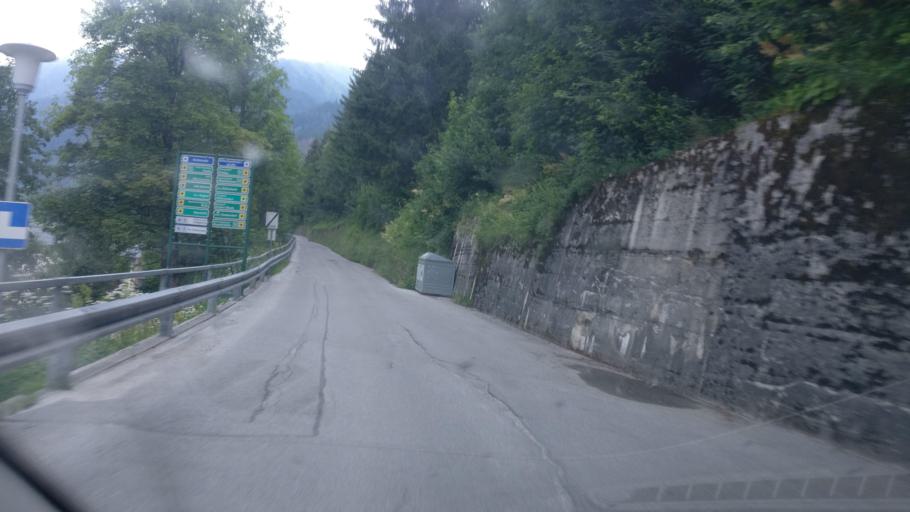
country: AT
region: Salzburg
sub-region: Politischer Bezirk Sankt Johann im Pongau
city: Bad Gastein
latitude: 47.1193
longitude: 13.1439
